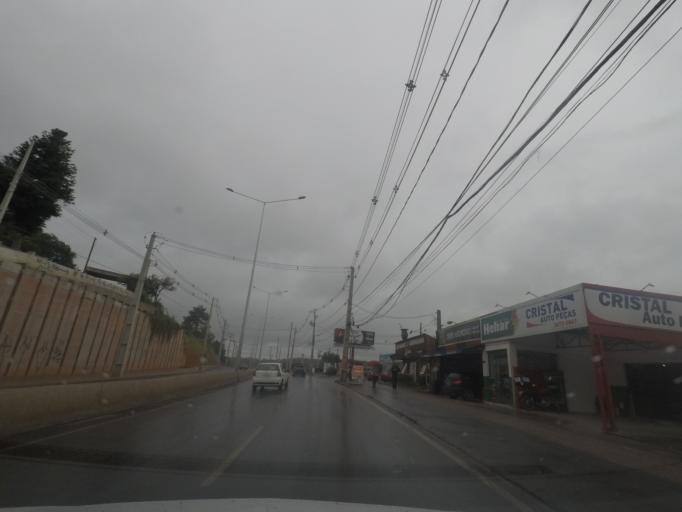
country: BR
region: Parana
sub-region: Piraquara
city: Piraquara
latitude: -25.4567
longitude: -49.0784
